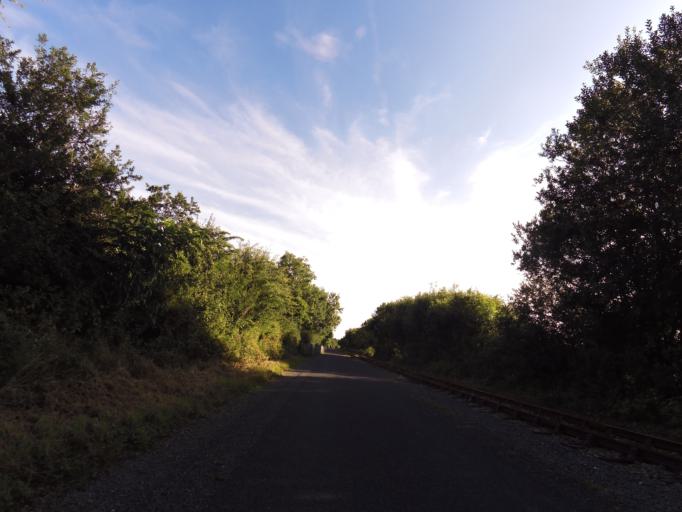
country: IE
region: Leinster
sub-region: Kilkenny
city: Mooncoin
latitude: 52.2524
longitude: -7.1935
